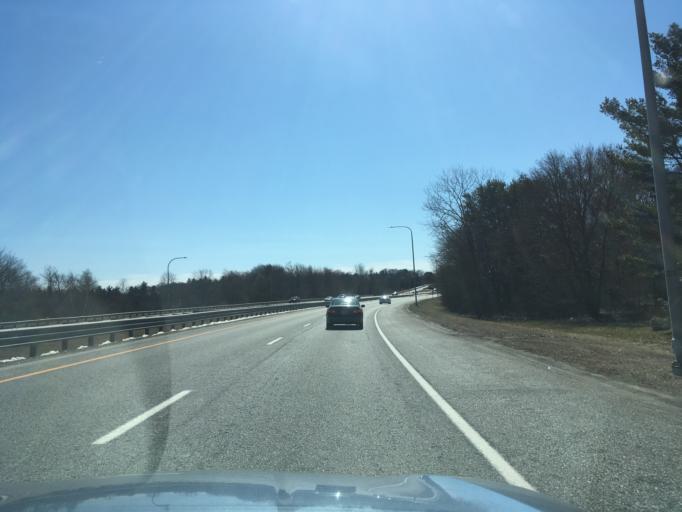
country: US
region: Rhode Island
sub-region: Kent County
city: East Greenwich
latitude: 41.6185
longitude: -71.4874
